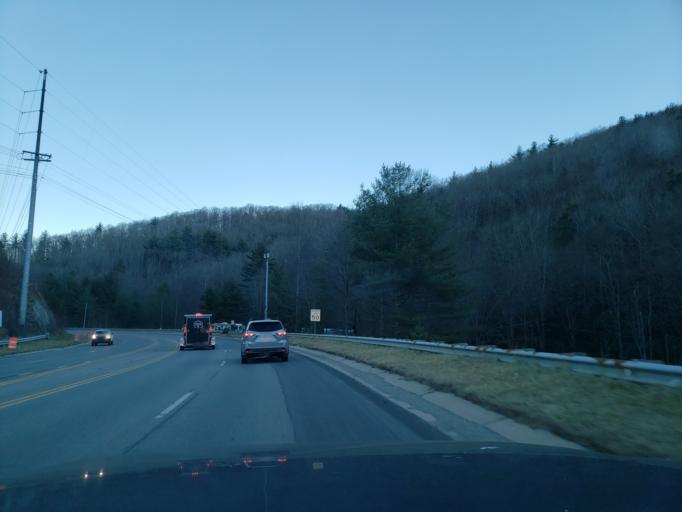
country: US
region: North Carolina
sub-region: Watauga County
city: Blowing Rock
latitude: 36.1702
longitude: -81.6458
